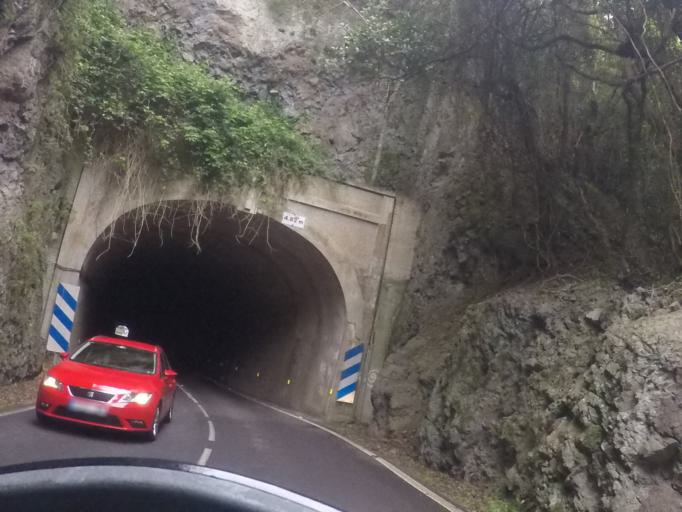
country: ES
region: Canary Islands
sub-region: Provincia de Santa Cruz de Tenerife
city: Santa Cruz de Tenerife
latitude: 28.5481
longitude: -16.2032
